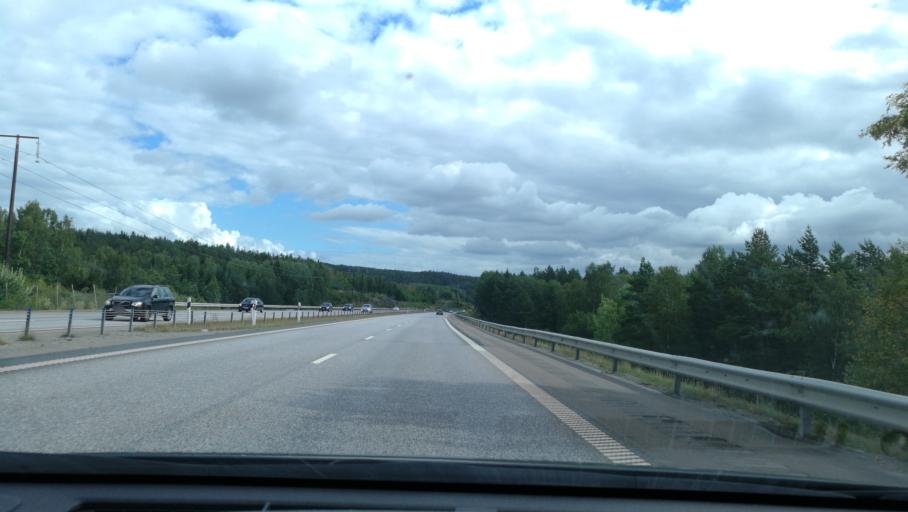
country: SE
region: OEstergoetland
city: Lindo
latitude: 58.6738
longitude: 16.2546
